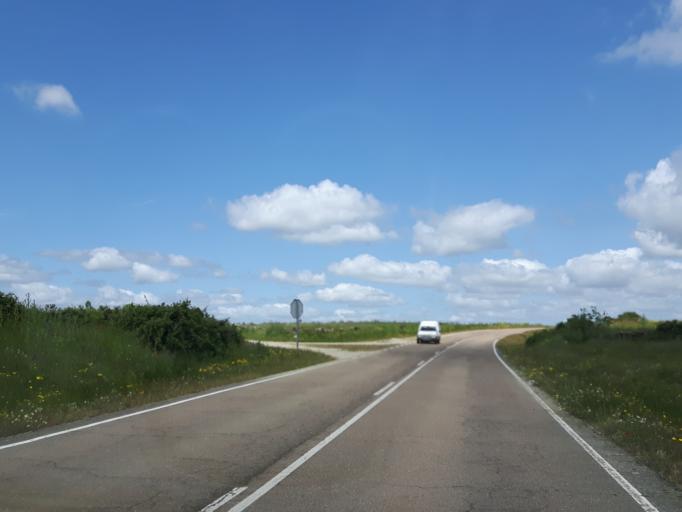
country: ES
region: Castille and Leon
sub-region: Provincia de Salamanca
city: Villar de la Yegua
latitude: 40.7262
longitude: -6.7099
